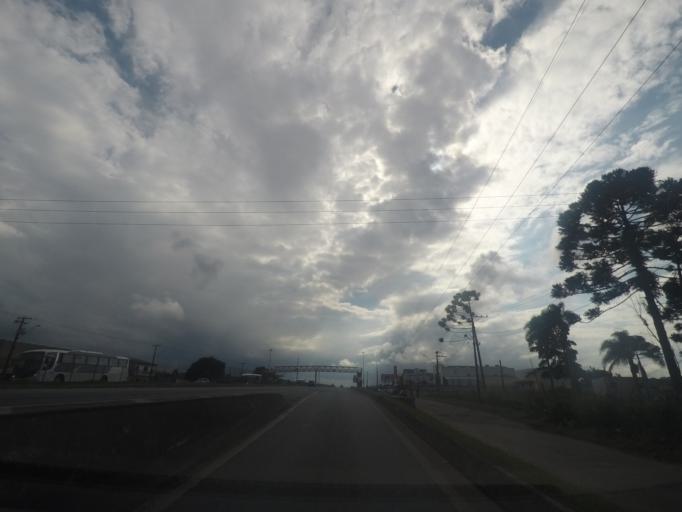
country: BR
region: Parana
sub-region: Piraquara
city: Piraquara
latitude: -25.5256
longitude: -49.0958
